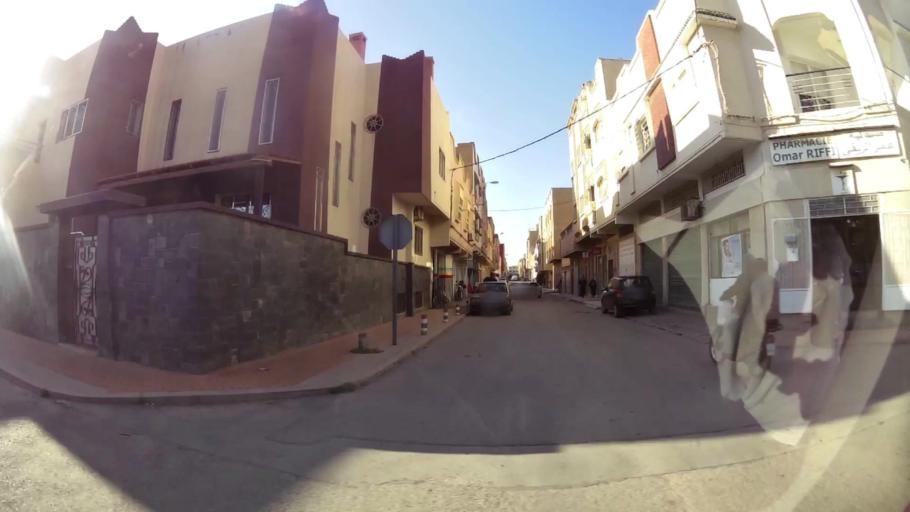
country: MA
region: Oriental
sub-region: Oujda-Angad
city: Oujda
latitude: 34.6911
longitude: -1.9159
